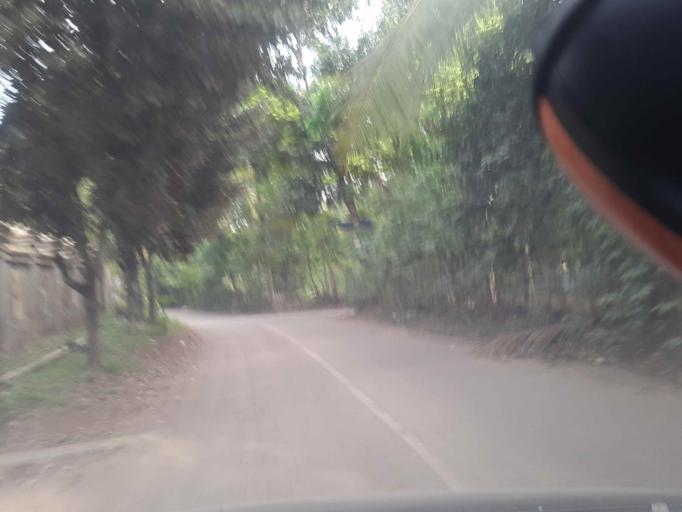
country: ID
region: Banten
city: Pekijing
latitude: -6.0734
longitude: 106.0911
